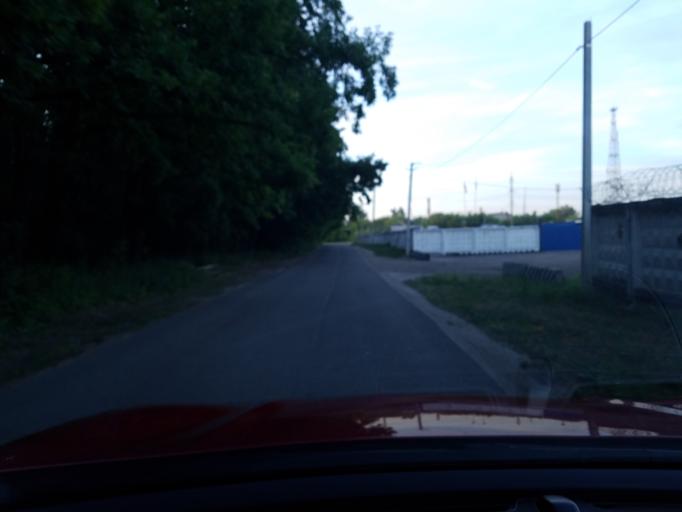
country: RU
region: Orjol
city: Znamenka
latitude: 52.9132
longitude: 36.0068
